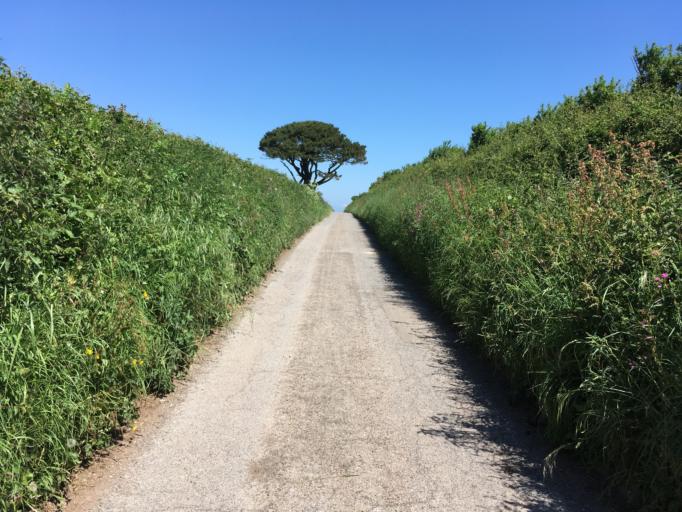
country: GB
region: England
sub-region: Devon
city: Dartmouth
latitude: 50.3478
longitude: -3.5421
